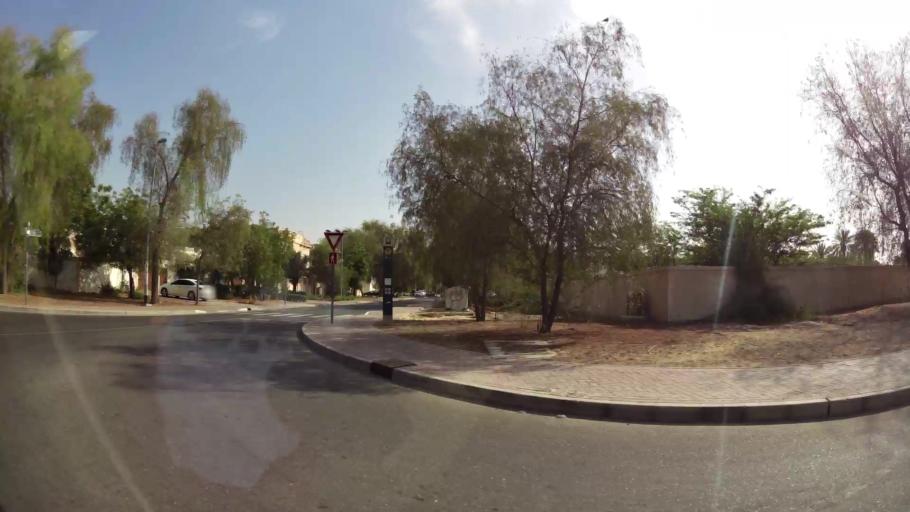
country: AE
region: Ash Shariqah
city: Sharjah
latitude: 25.2263
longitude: 55.3893
